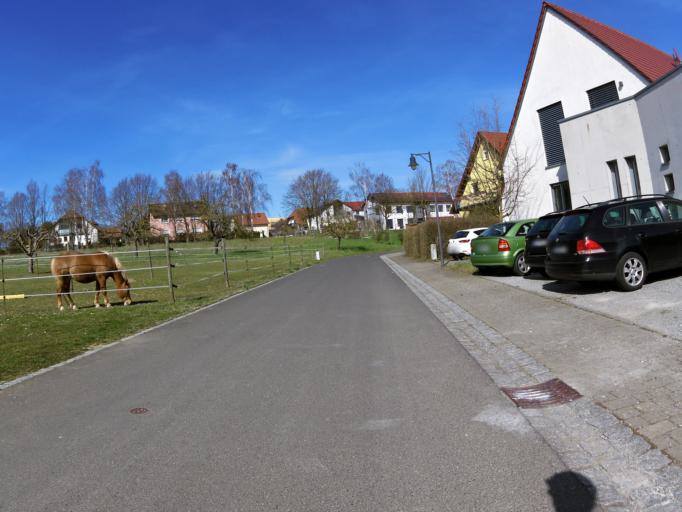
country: DE
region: Bavaria
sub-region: Regierungsbezirk Unterfranken
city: Biebelried
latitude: 49.7962
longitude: 10.0885
